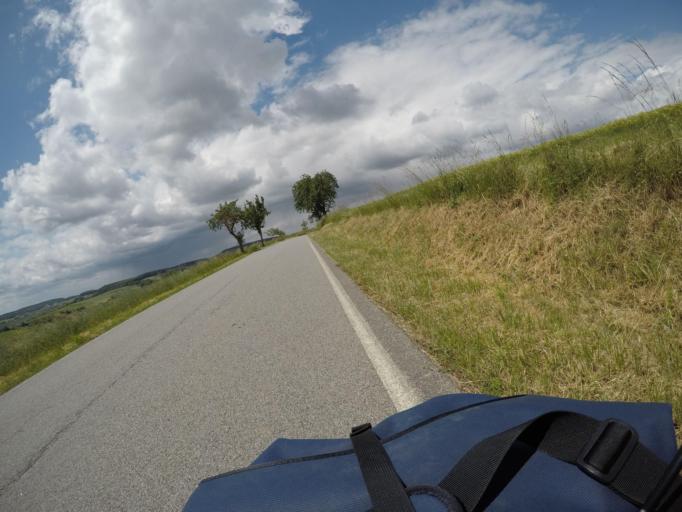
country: DE
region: Baden-Wuerttemberg
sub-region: Regierungsbezirk Stuttgart
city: Ittlingen
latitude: 49.1943
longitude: 8.8734
